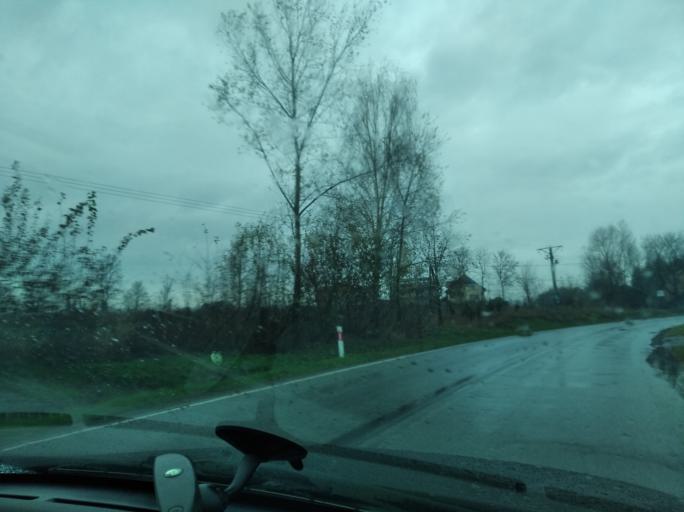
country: PL
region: Subcarpathian Voivodeship
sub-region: Powiat lancucki
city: Albigowa
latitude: 50.0336
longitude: 22.2283
